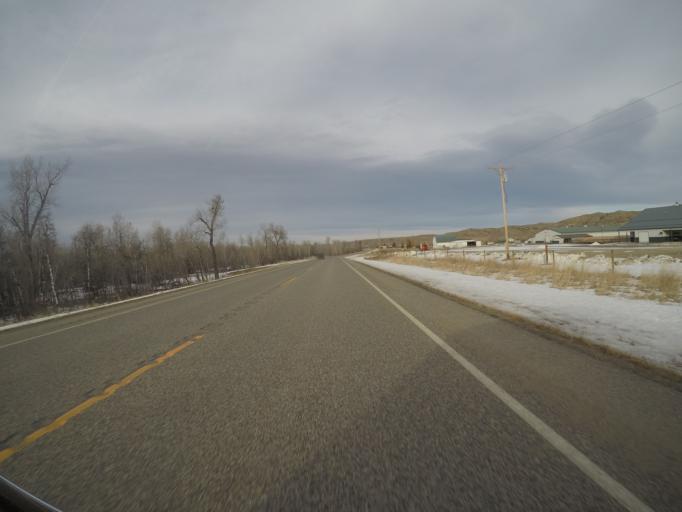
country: US
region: Montana
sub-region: Stillwater County
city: Absarokee
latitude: 45.4592
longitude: -109.4489
